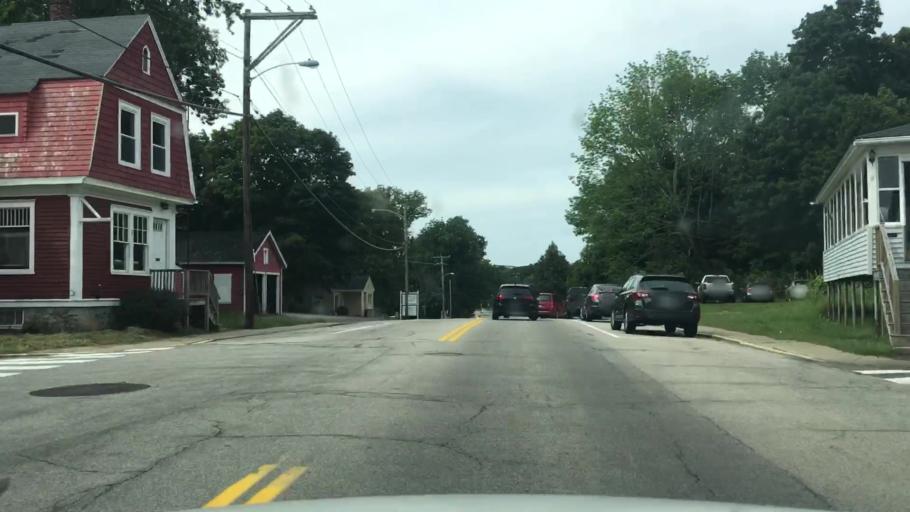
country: US
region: Maine
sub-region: York County
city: Kittery
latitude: 43.0864
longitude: -70.7456
